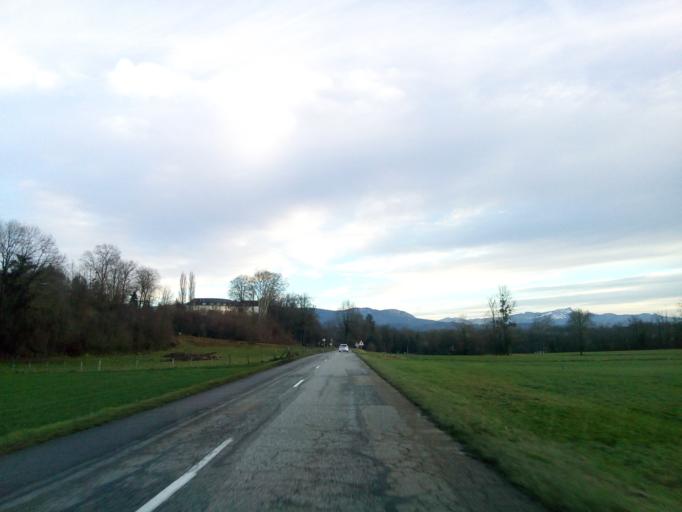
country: FR
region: Rhone-Alpes
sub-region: Departement de la Savoie
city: Le Pont-de-Beauvoisin
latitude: 45.5625
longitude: 5.6724
